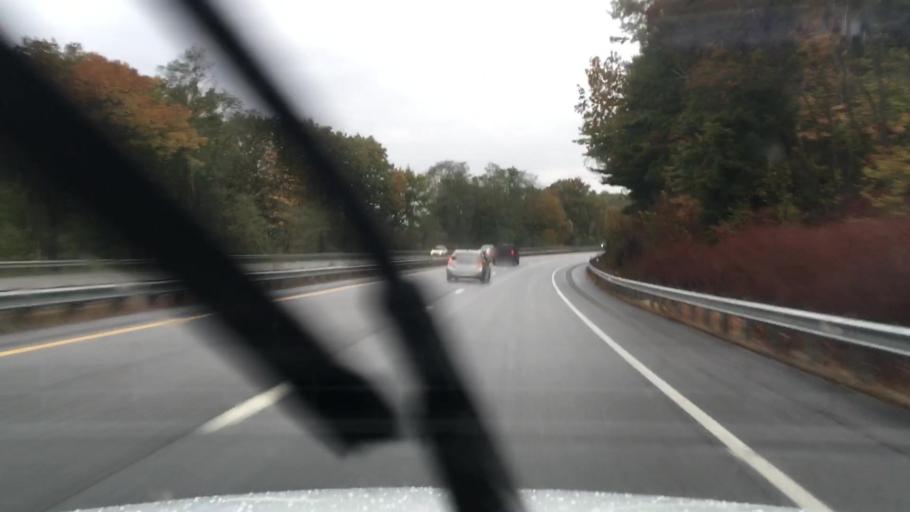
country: US
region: New Hampshire
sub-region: Strafford County
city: Dover
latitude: 43.1754
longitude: -70.8688
